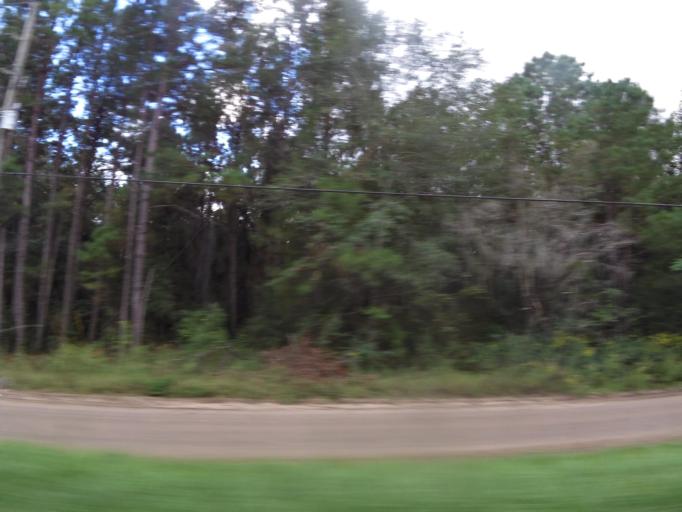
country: US
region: Georgia
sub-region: Liberty County
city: Midway
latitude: 31.8429
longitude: -81.4140
